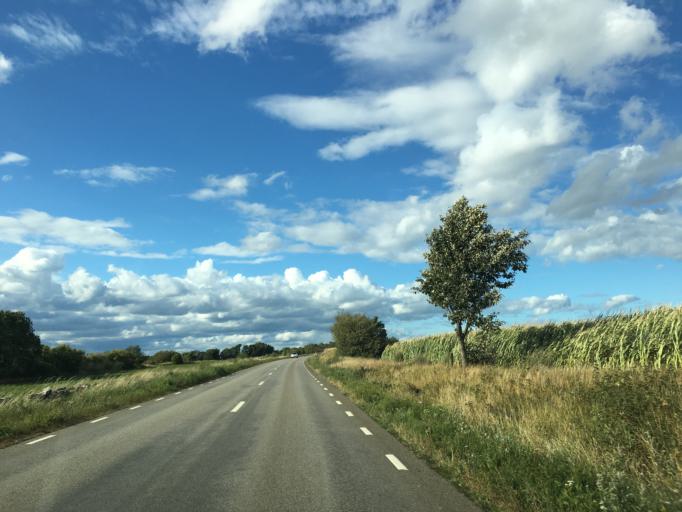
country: SE
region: Kalmar
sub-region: Morbylanga Kommun
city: Moerbylanga
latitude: 56.4741
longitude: 16.4295
